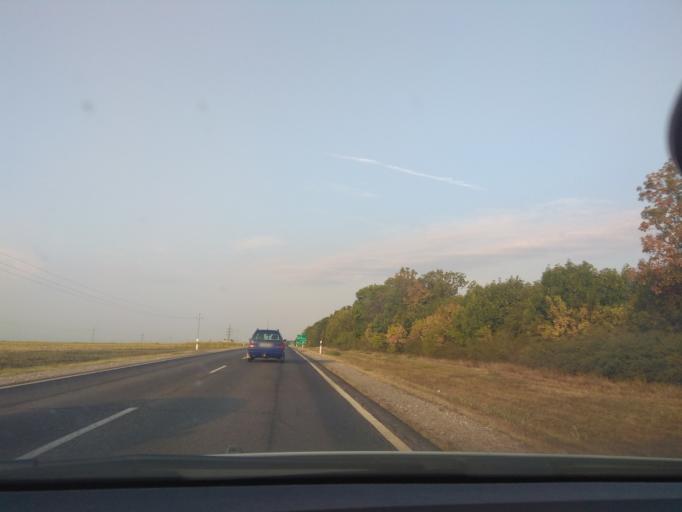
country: HU
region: Borsod-Abauj-Zemplen
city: Mezokovesd
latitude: 47.8260
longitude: 20.6089
